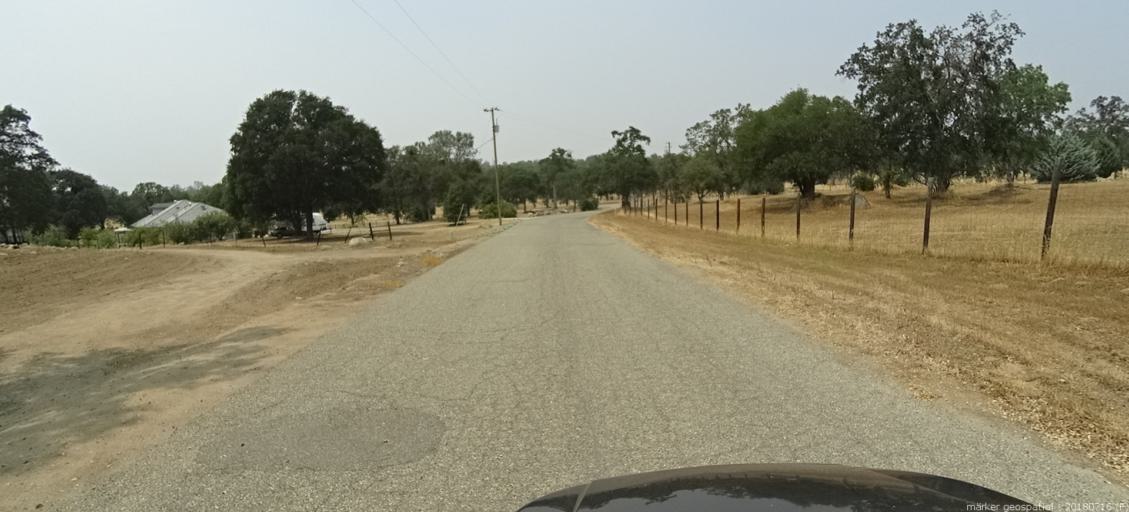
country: US
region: California
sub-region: Madera County
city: Yosemite Lakes
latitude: 37.2395
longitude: -119.8029
